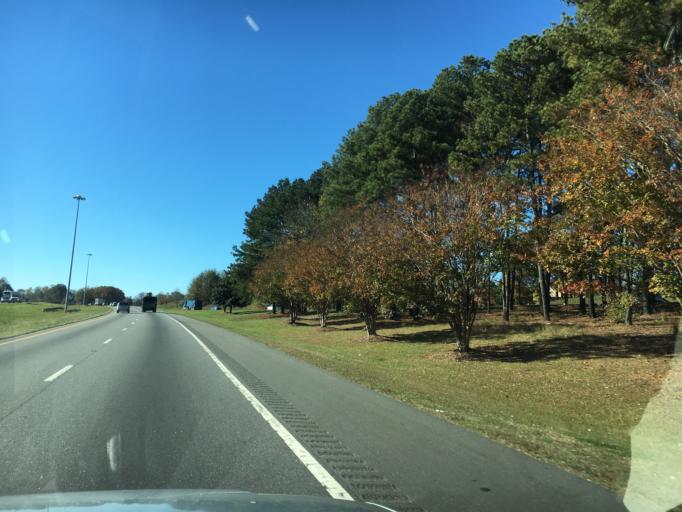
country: US
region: North Carolina
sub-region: Catawba County
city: Hickory
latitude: 35.7138
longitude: -81.3136
